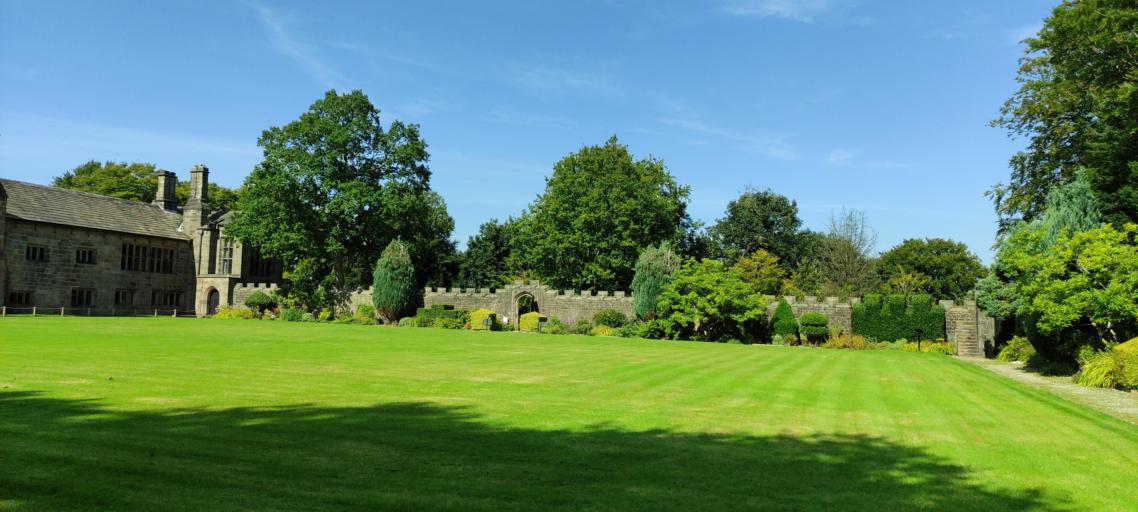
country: GB
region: England
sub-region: Blackburn with Darwen
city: Blackburn
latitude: 53.7329
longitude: -2.5719
